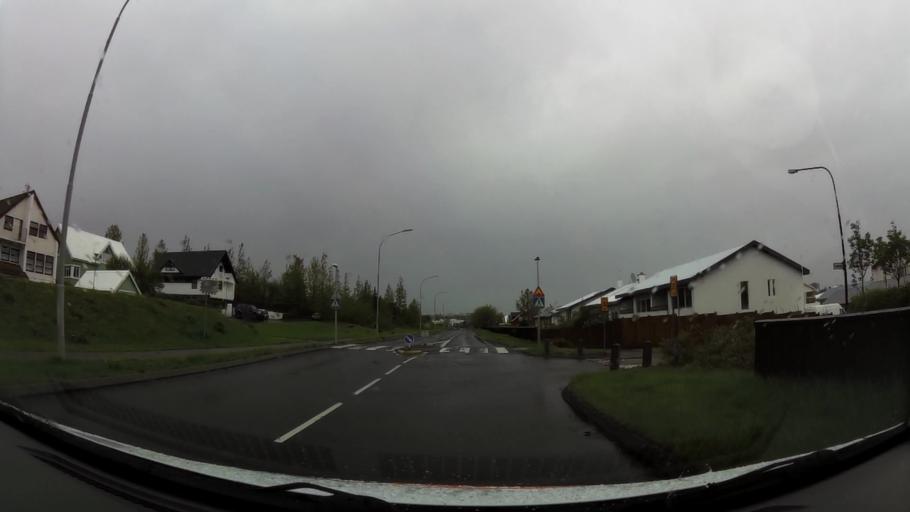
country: IS
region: Capital Region
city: Reykjavik
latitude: 64.0942
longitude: -21.8328
